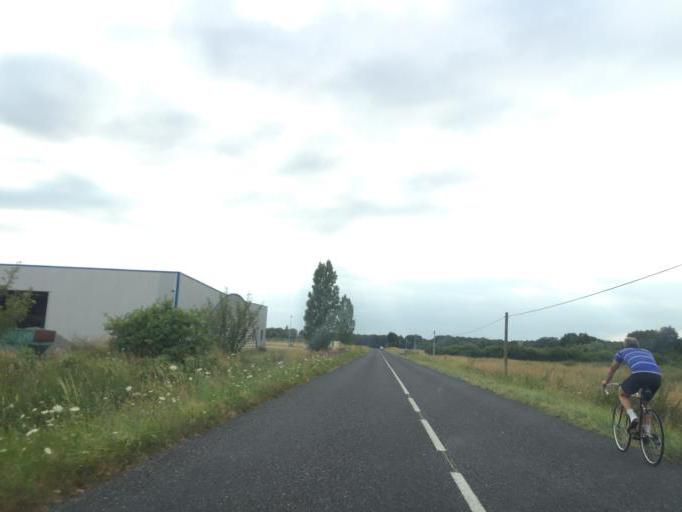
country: FR
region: Auvergne
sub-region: Departement de l'Allier
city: Toulon-sur-Allier
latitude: 46.5383
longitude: 3.4281
